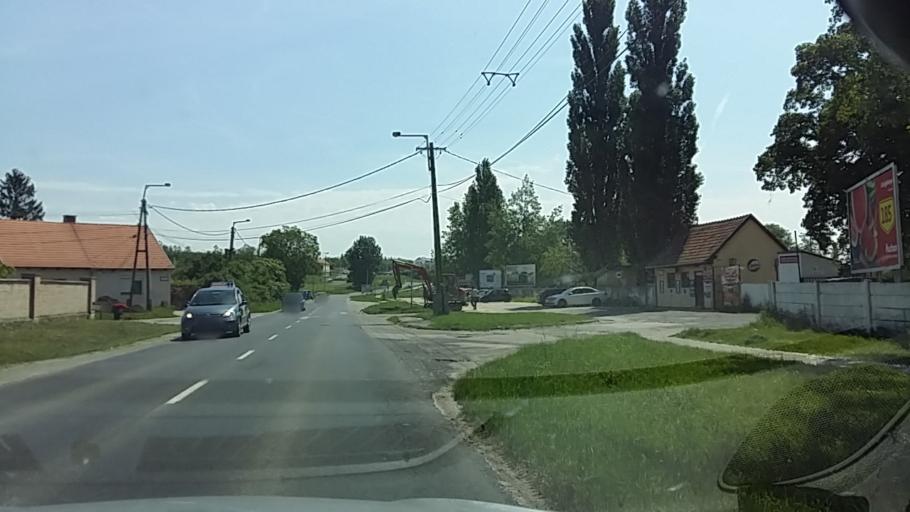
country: HU
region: Gyor-Moson-Sopron
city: Sopron
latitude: 47.6826
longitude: 16.6092
